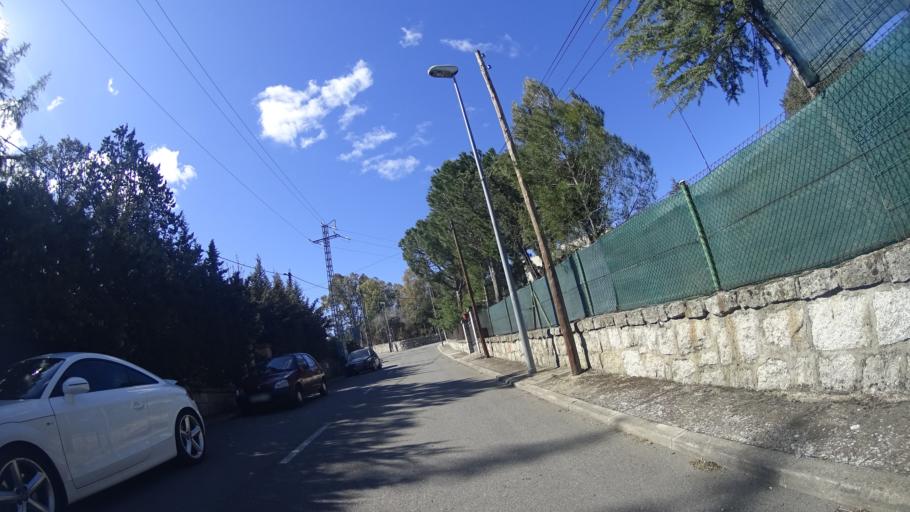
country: ES
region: Madrid
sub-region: Provincia de Madrid
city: Las Matas
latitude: 40.5569
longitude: -3.8918
